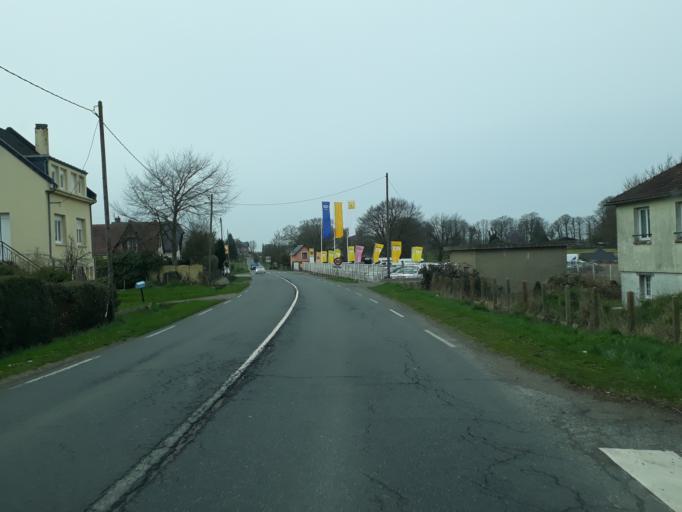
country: FR
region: Haute-Normandie
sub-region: Departement de la Seine-Maritime
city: Beuzeville-la-Grenier
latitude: 49.5931
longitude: 0.4263
